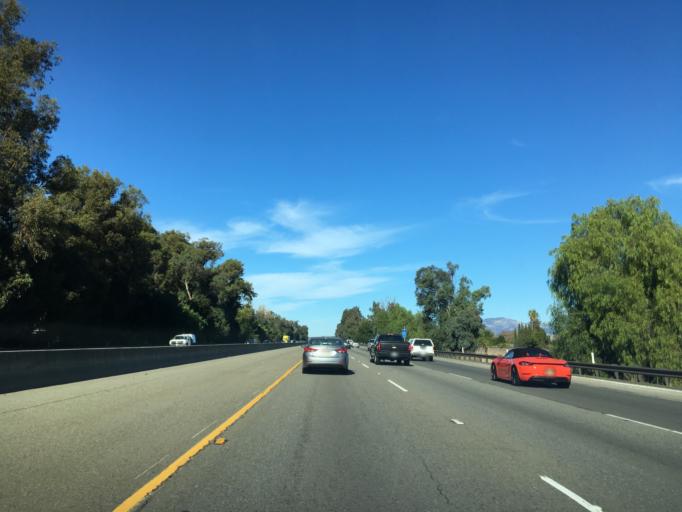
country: US
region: California
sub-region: Alameda County
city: Dublin
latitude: 37.6782
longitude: -121.9137
